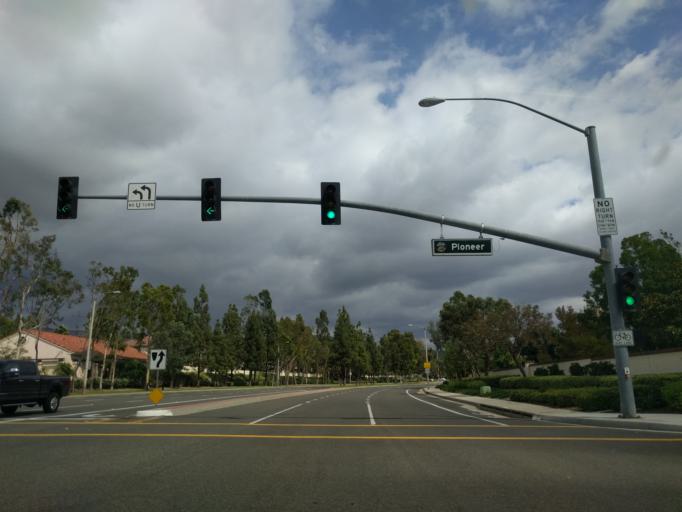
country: US
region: California
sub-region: Orange County
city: North Tustin
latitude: 33.7481
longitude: -117.7712
